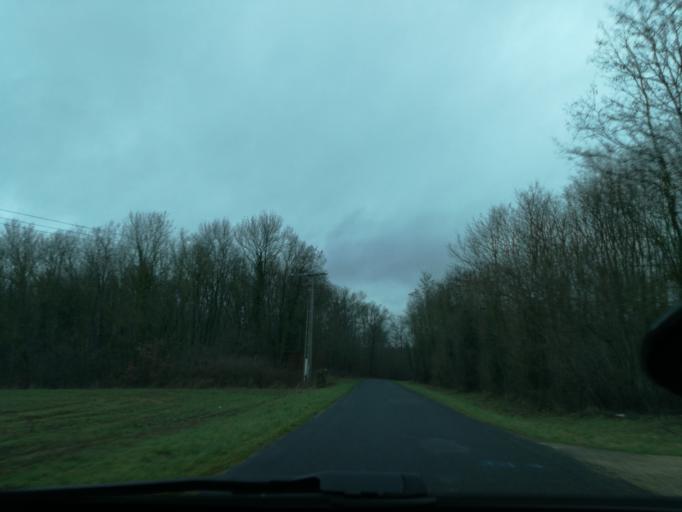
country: FR
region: Lorraine
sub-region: Departement de la Meuse
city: Revigny-sur-Ornain
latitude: 48.8495
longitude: 5.0574
